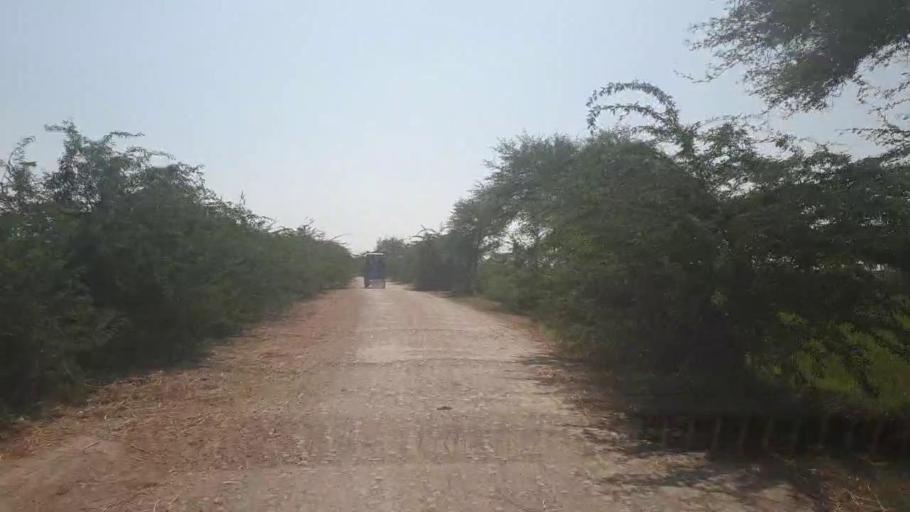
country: PK
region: Sindh
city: Badin
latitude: 24.6431
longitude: 68.9119
